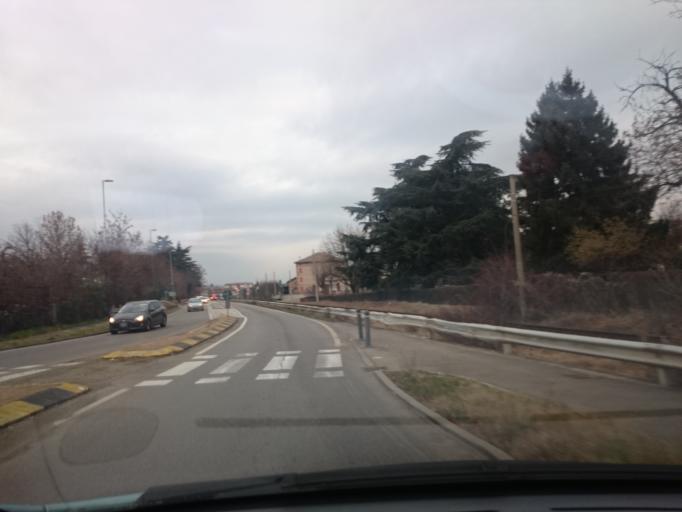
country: IT
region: Emilia-Romagna
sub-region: Provincia di Reggio Emilia
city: Scandiano
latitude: 44.5980
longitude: 10.7024
